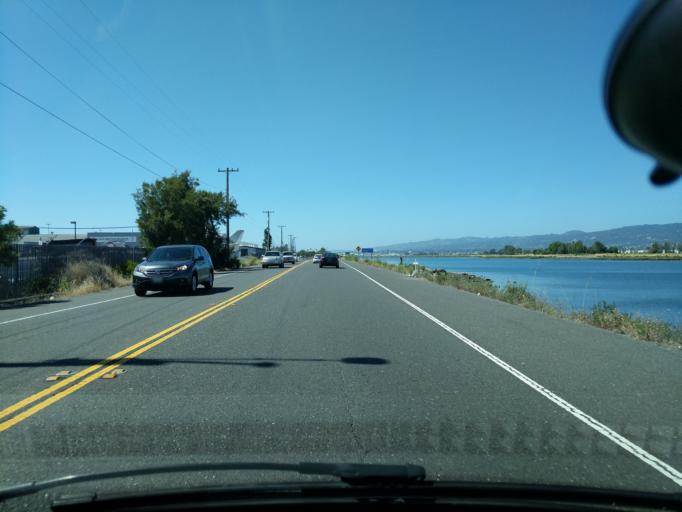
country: US
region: California
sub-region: Alameda County
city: Alameda
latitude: 37.7323
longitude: -122.2111
